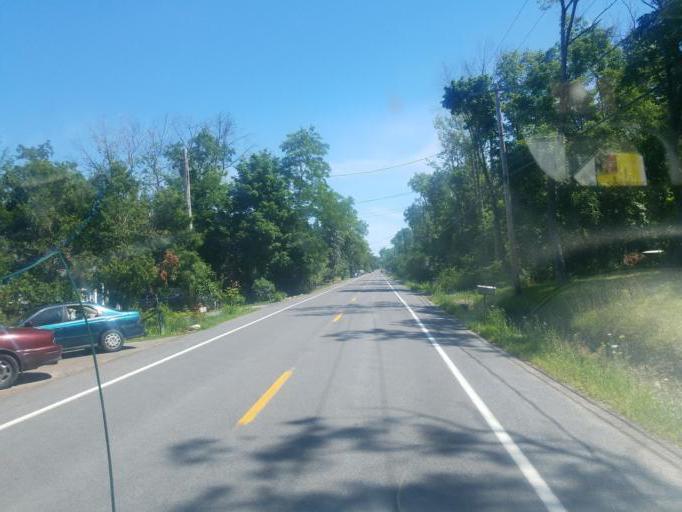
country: US
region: New York
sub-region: Ontario County
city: Canandaigua
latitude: 42.7829
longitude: -77.2846
